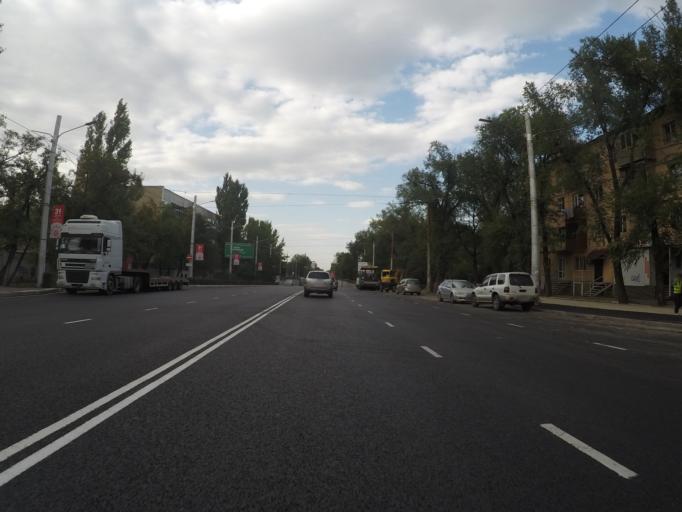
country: KG
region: Chuy
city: Bishkek
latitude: 42.8603
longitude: 74.5870
